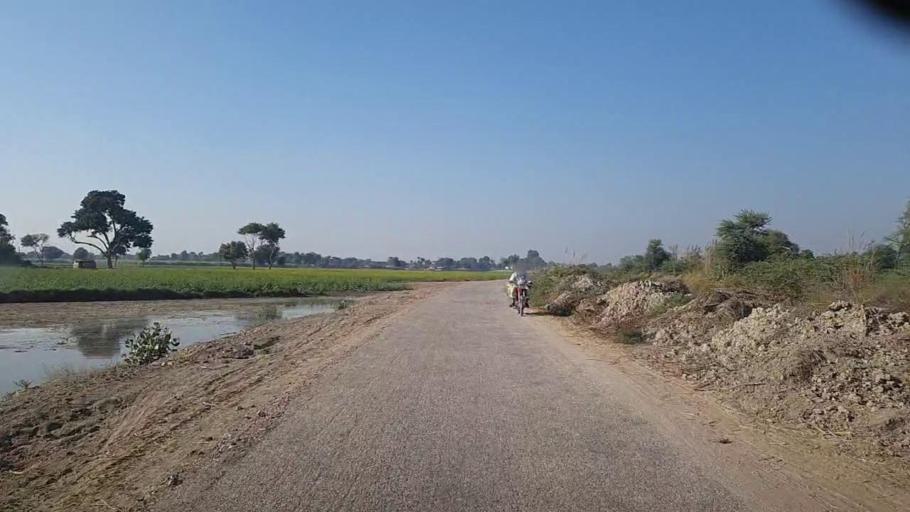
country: PK
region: Sindh
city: Darya Khan Marri
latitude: 26.6903
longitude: 68.3508
